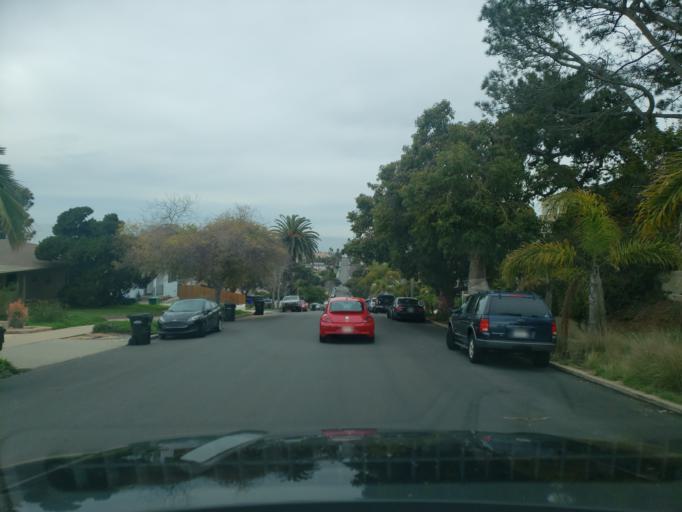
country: US
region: California
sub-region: San Diego County
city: Coronado
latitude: 32.7378
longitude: -117.2489
